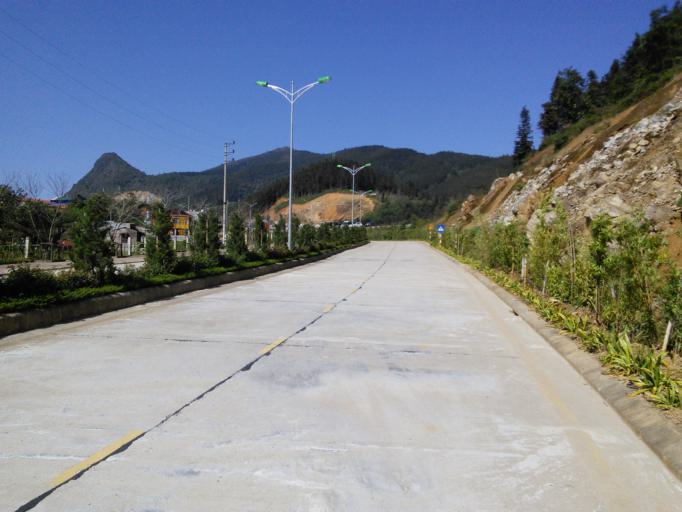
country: VN
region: Lao Cai
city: Sa Pa
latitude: 22.3428
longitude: 103.8217
